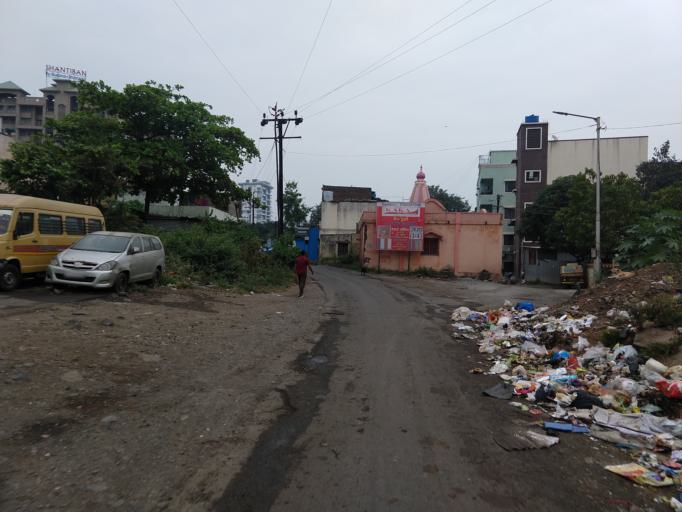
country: IN
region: Maharashtra
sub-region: Pune Division
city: Pune
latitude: 18.4543
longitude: 73.8847
